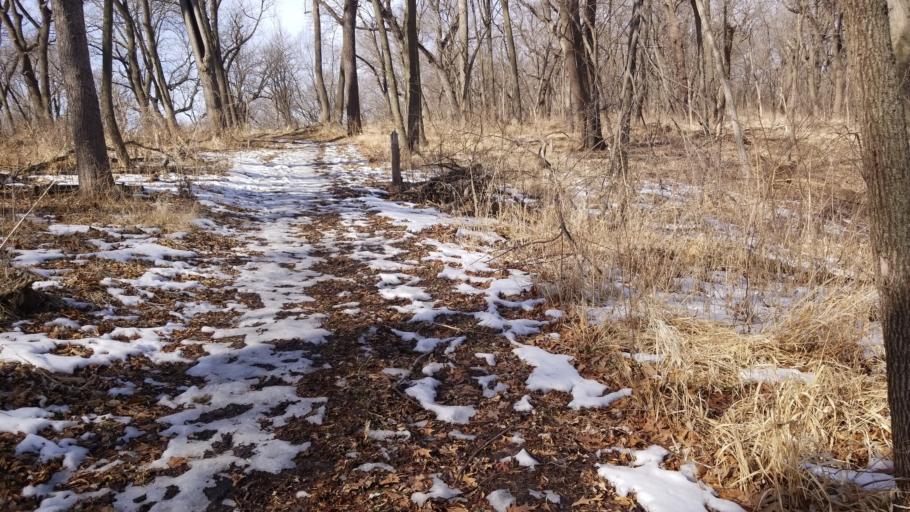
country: US
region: Nebraska
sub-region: Sarpy County
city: Bellevue
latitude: 41.1716
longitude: -95.9004
